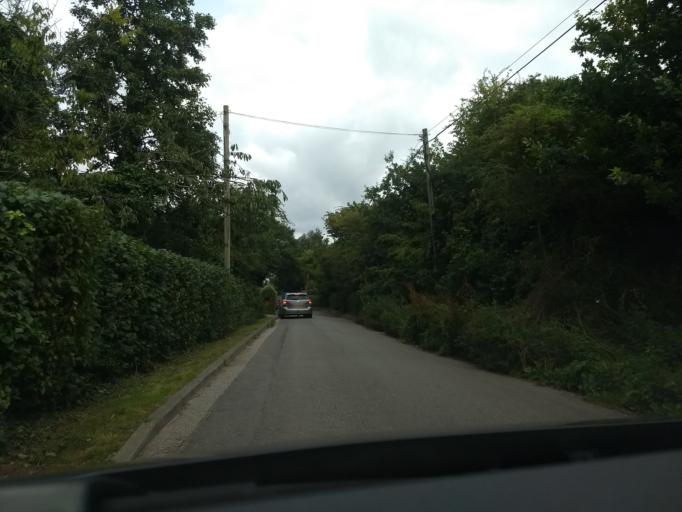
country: GB
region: England
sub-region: Suffolk
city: Shotley Gate
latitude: 51.9930
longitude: 1.2130
